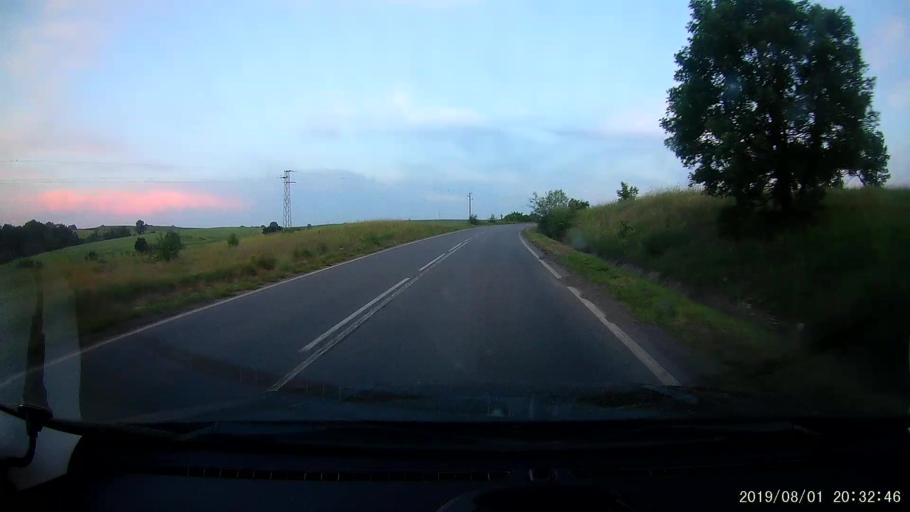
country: BG
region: Yambol
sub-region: Obshtina Elkhovo
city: Elkhovo
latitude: 42.1170
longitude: 26.5309
